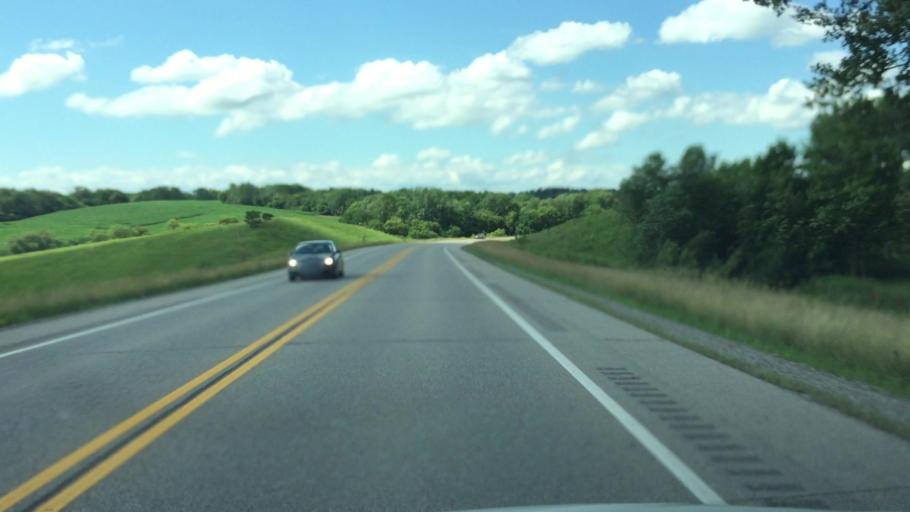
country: US
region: Iowa
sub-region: Johnson County
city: Solon
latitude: 41.7654
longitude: -91.4818
